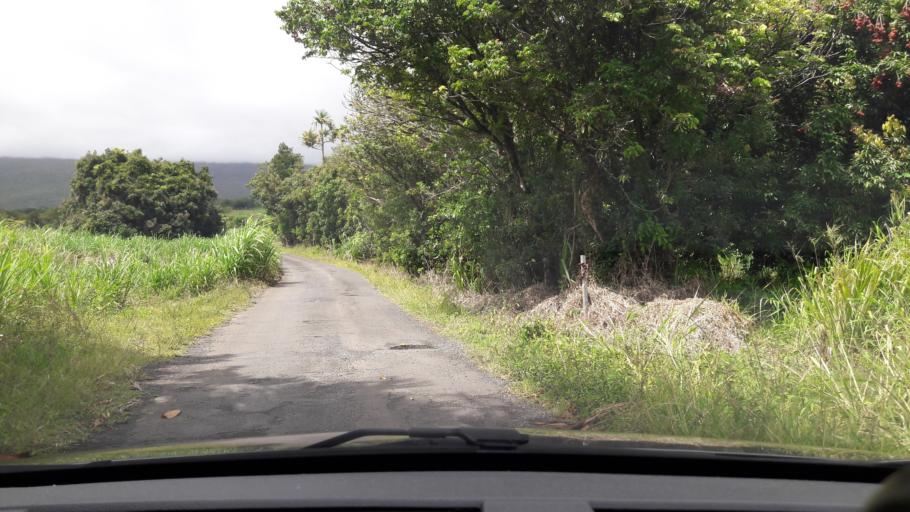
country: RE
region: Reunion
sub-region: Reunion
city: Saint-Benoit
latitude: -21.0968
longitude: 55.6989
